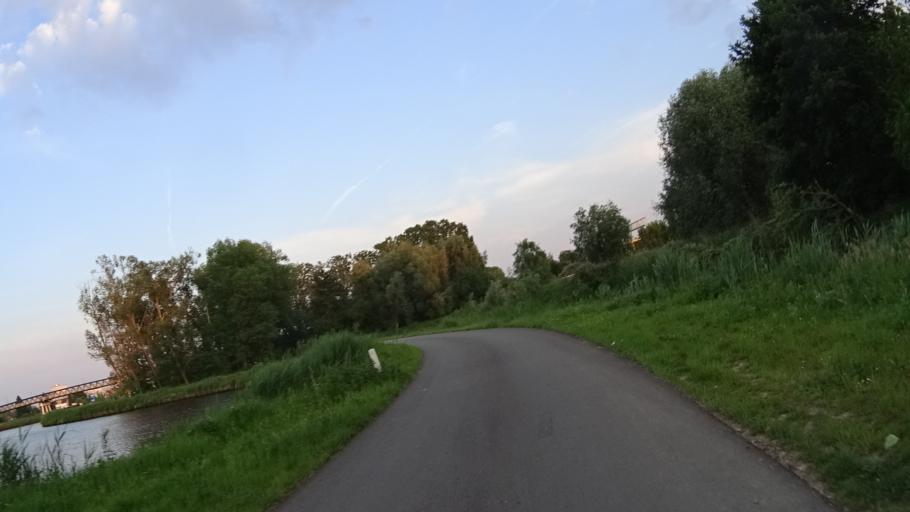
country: NL
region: North Brabant
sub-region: Gemeente Veghel
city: Eerde
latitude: 51.6172
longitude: 5.5129
